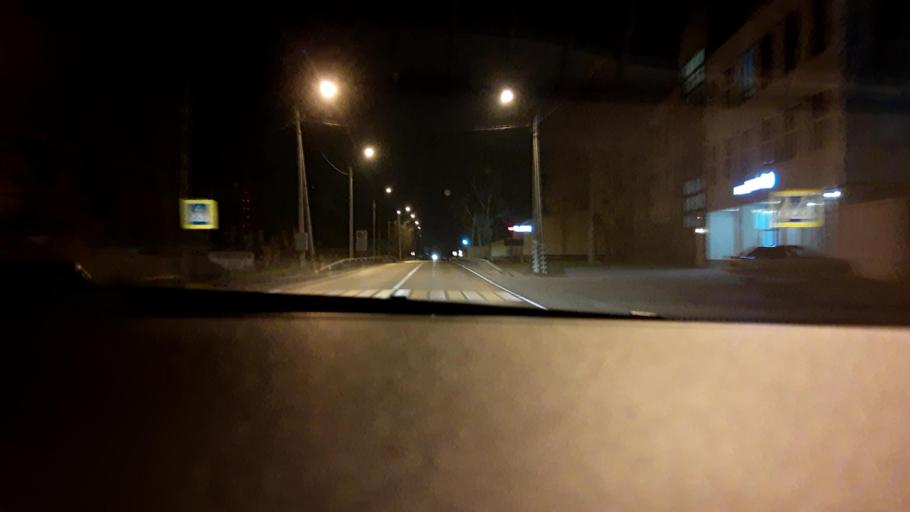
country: RU
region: Nizjnij Novgorod
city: Novaya Balakhna
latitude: 56.4903
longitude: 43.5962
